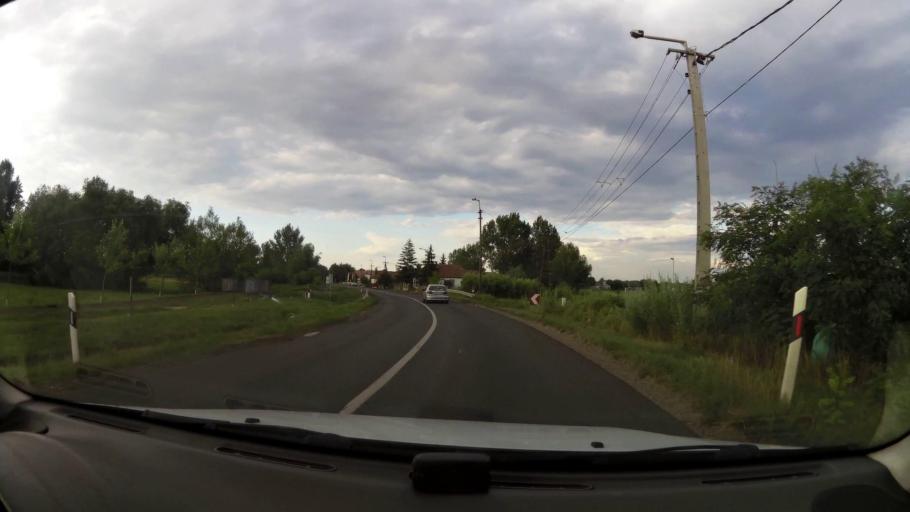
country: HU
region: Pest
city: Tapioszecso
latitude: 47.4489
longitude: 19.5895
